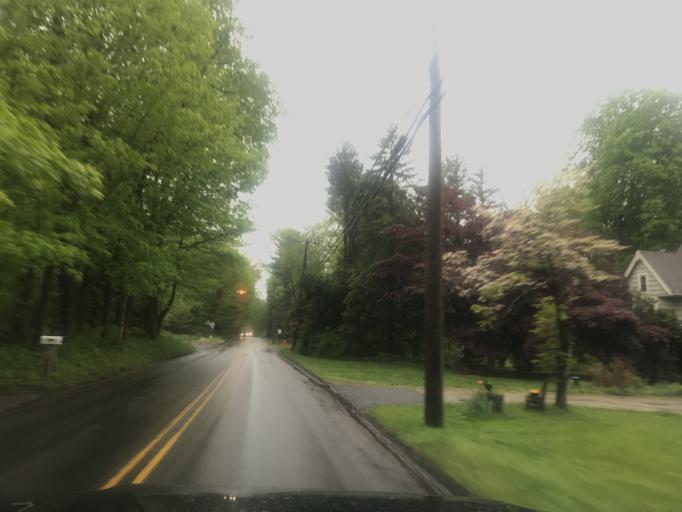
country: US
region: Connecticut
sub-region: Fairfield County
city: Bethel
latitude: 41.3125
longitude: -73.3555
